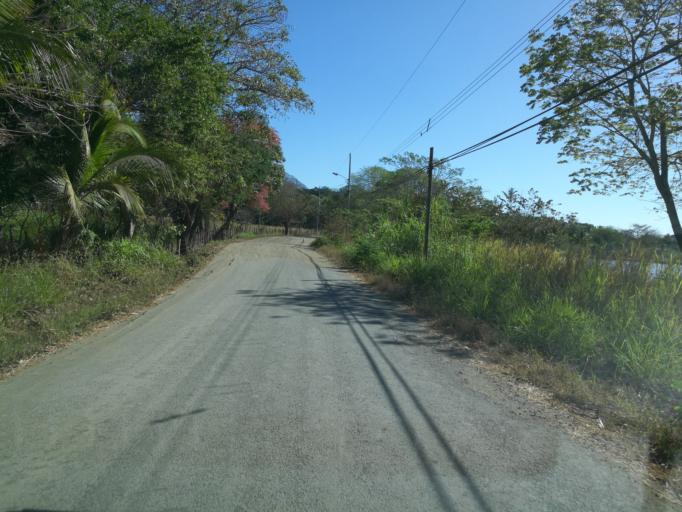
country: CR
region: Puntarenas
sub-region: Canton Central de Puntarenas
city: Puntarenas
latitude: 10.0910
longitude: -84.9648
